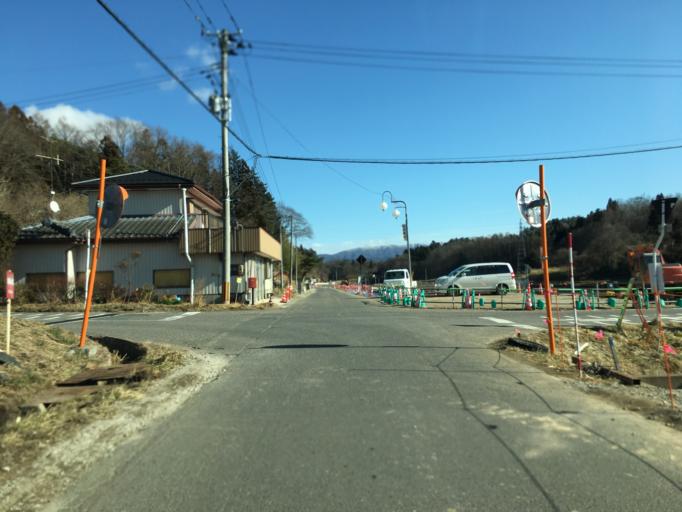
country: JP
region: Fukushima
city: Funehikimachi-funehiki
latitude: 37.4142
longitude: 140.5787
